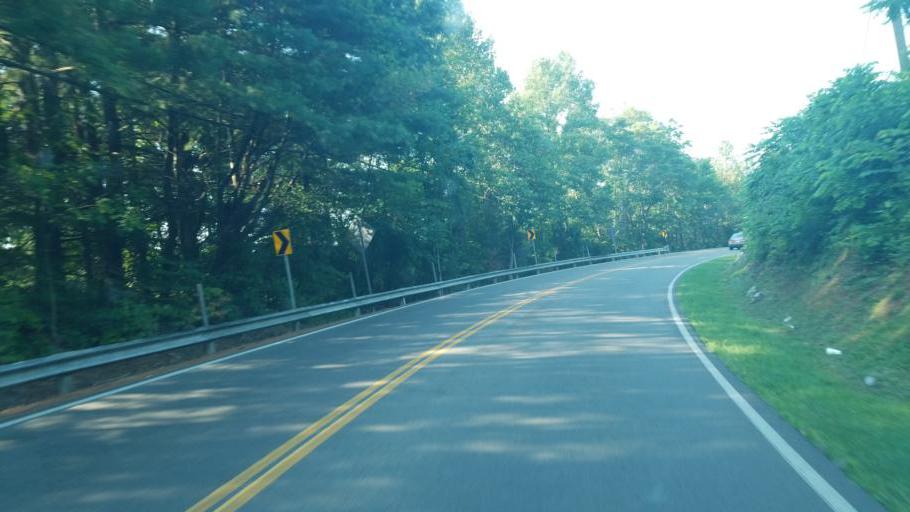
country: US
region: Tennessee
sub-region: Sullivan County
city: Bluff City
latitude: 36.4623
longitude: -82.2734
